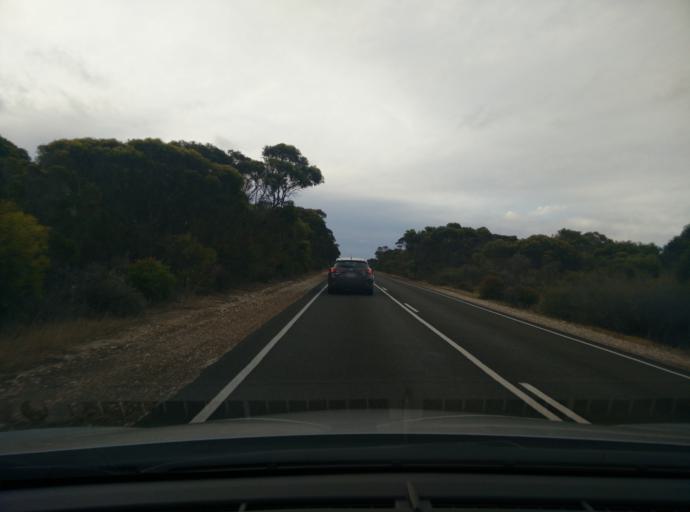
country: AU
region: South Australia
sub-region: Kangaroo Island
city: Kingscote
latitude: -35.7968
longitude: 137.6609
